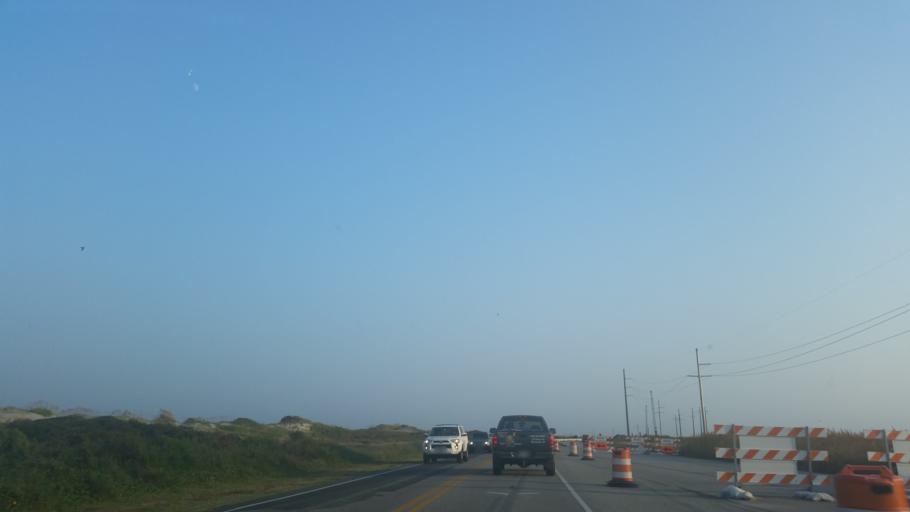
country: US
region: North Carolina
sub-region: Dare County
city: Wanchese
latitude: 35.6904
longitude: -75.4846
